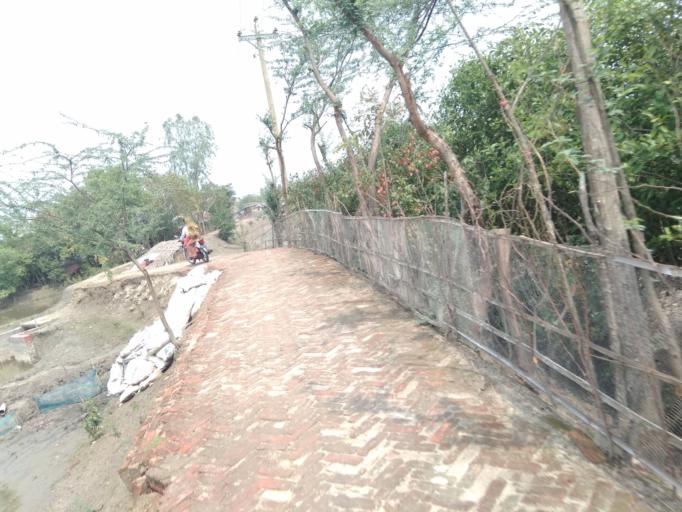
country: IN
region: West Bengal
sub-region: North 24 Parganas
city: Taki
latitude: 22.2780
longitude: 89.2845
